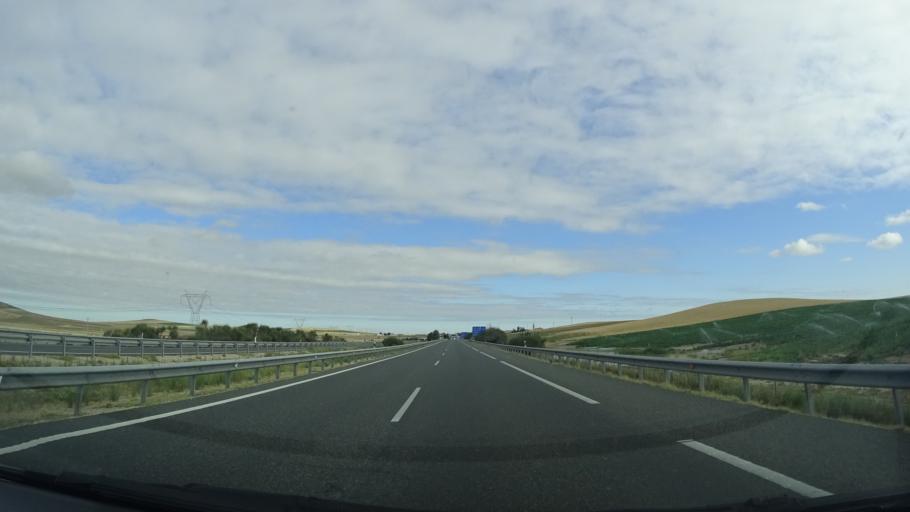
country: ES
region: Castille and Leon
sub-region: Provincia de Valladolid
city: Ataquines
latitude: 41.1636
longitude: -4.7985
